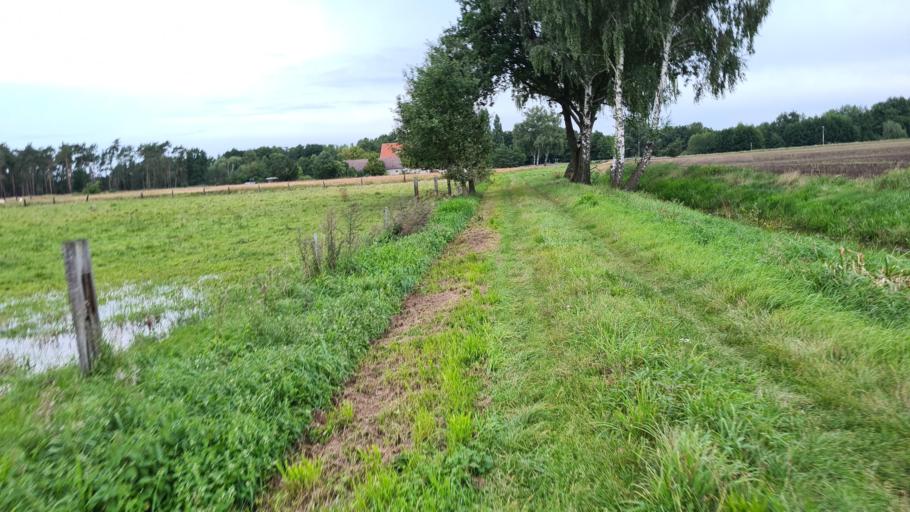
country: DE
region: Brandenburg
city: Bad Liebenwerda
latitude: 51.5454
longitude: 13.3525
